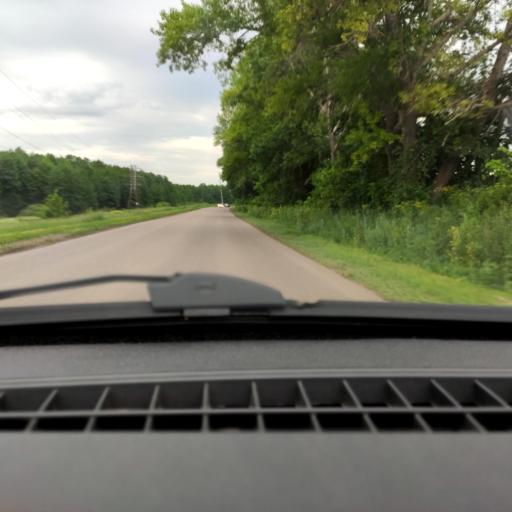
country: RU
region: Bashkortostan
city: Chishmy
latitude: 54.5944
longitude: 55.4478
